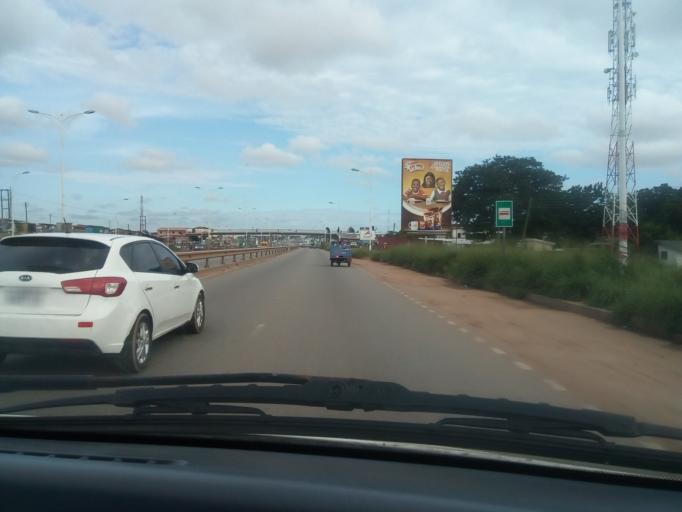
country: GH
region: Greater Accra
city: Dome
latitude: 5.6547
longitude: -0.2613
